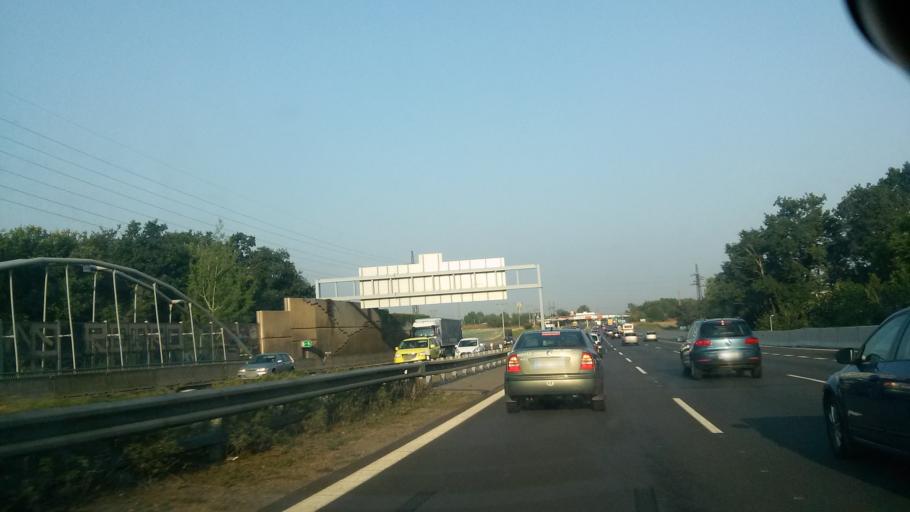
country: CZ
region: Central Bohemia
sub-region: Okres Praha-Zapad
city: Pruhonice
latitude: 50.0080
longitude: 14.5527
